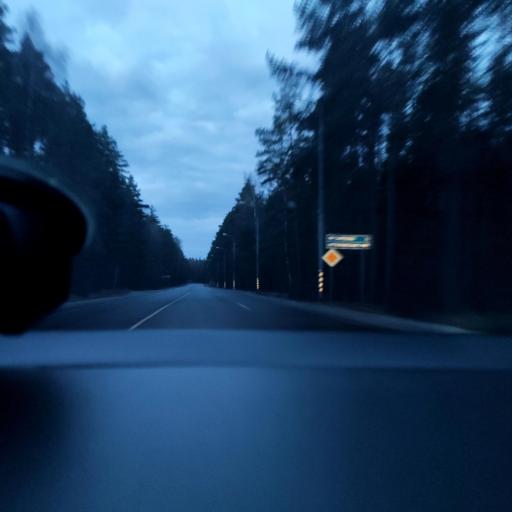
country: RU
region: Moskovskaya
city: Krasnyy Tkach
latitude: 55.4138
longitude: 39.1732
